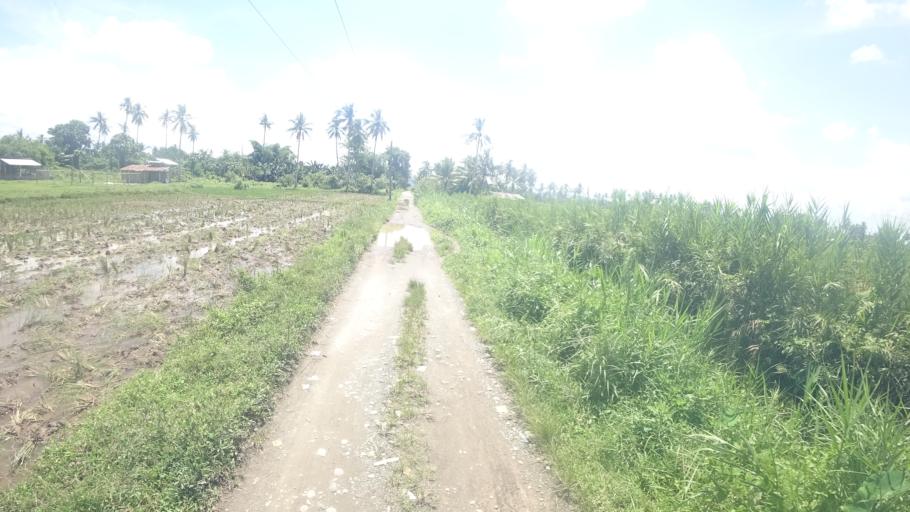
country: PH
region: Eastern Visayas
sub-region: Province of Leyte
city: Alangalang
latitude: 11.2294
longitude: 124.8427
